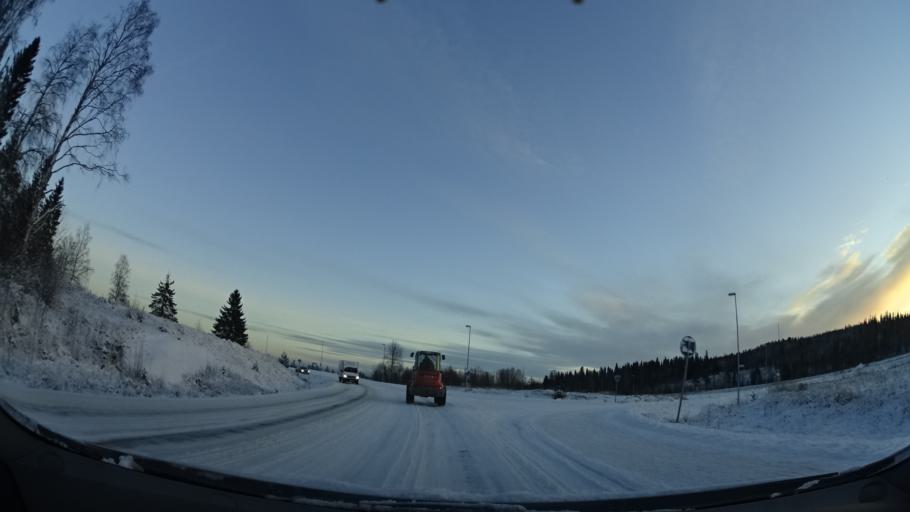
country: SE
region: Vaesterbotten
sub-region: Skelleftea Kommun
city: Kage
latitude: 64.8286
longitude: 21.0110
